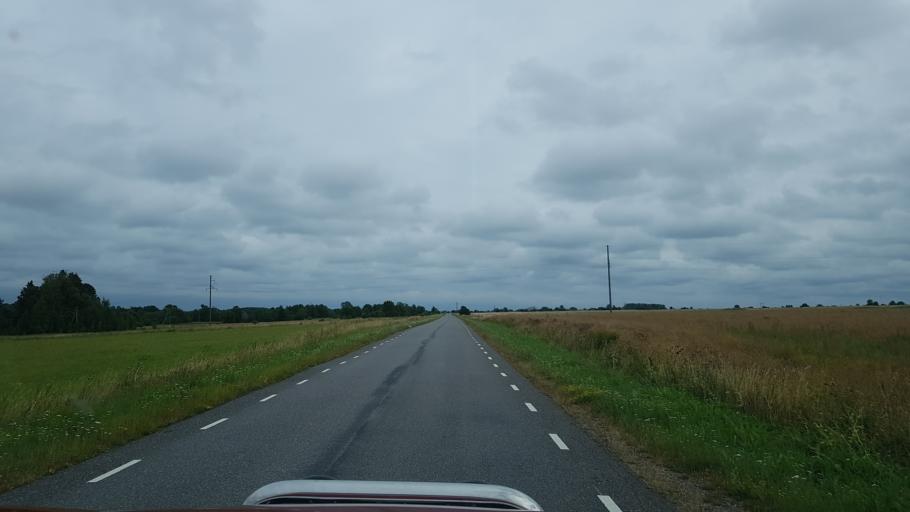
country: EE
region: Ida-Virumaa
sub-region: Puessi linn
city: Pussi
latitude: 59.4070
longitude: 27.0061
